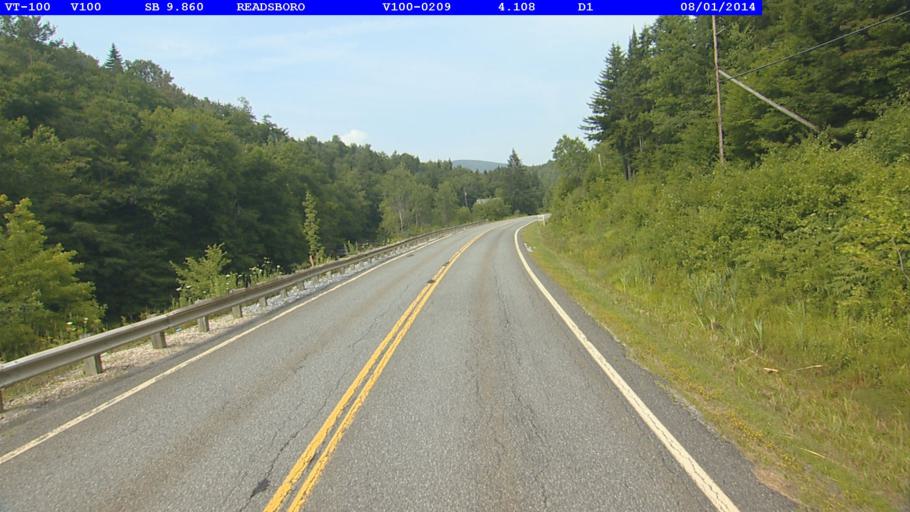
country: US
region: Massachusetts
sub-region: Berkshire County
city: North Adams
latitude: 42.8052
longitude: -72.9740
